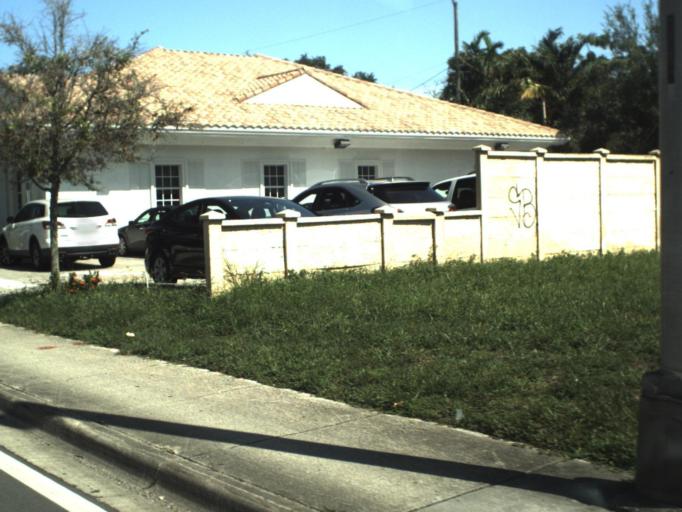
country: US
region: Florida
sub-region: Miami-Dade County
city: Ojus
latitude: 25.9472
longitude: -80.1534
